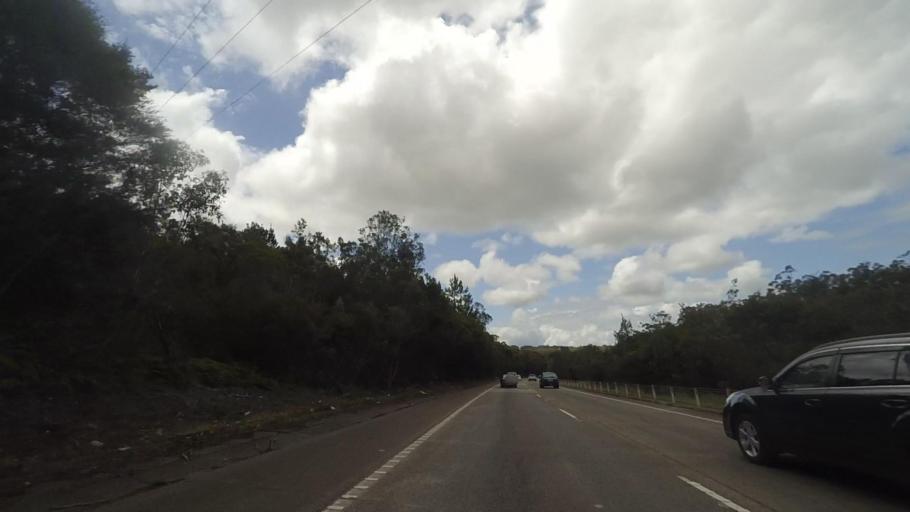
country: AU
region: New South Wales
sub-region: Gosford Shire
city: Narara
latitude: -33.3841
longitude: 151.2987
